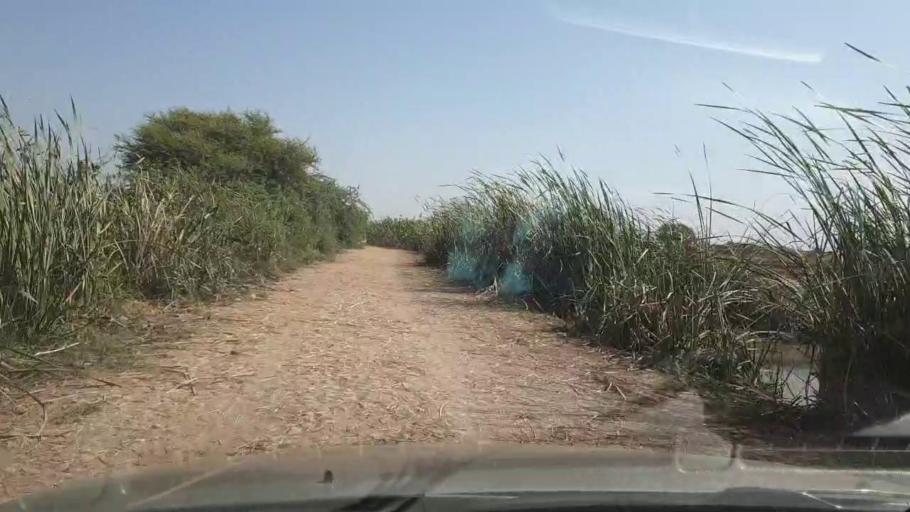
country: PK
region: Sindh
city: Daro Mehar
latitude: 24.9723
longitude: 68.1136
